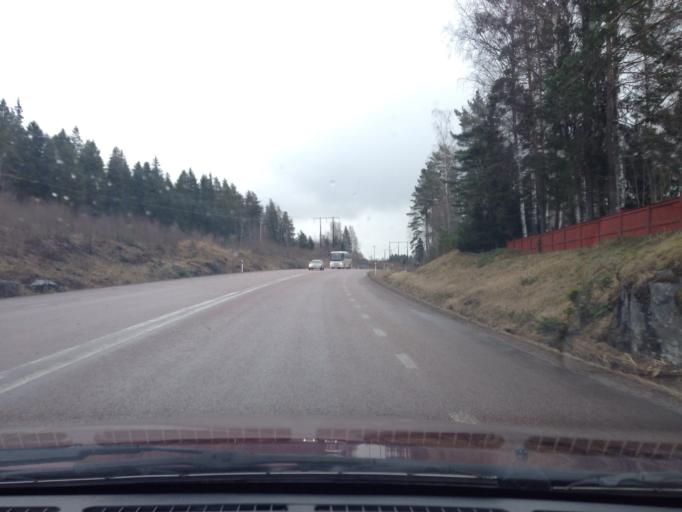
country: SE
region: Dalarna
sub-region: Ludvika Kommun
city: Ludvika
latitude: 60.1550
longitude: 15.2539
